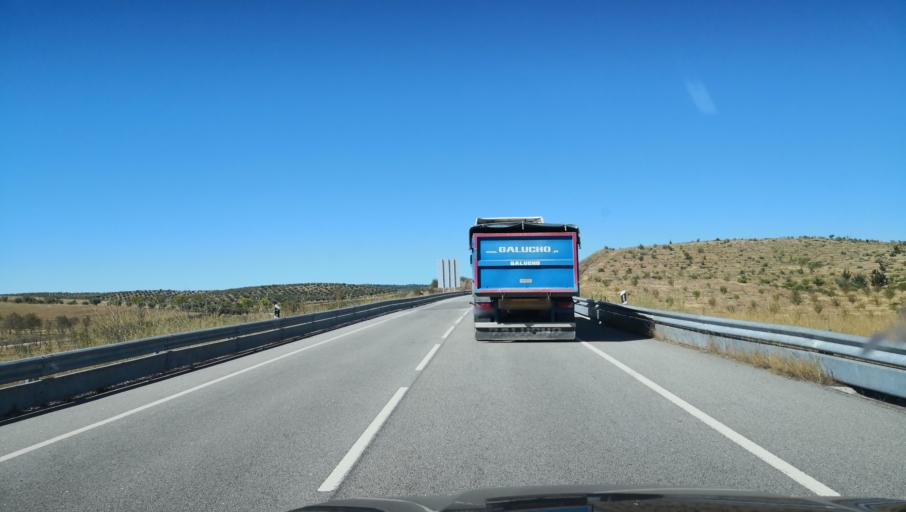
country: PT
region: Vila Real
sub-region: Valpacos
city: Valpacos
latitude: 41.5420
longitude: -7.2553
